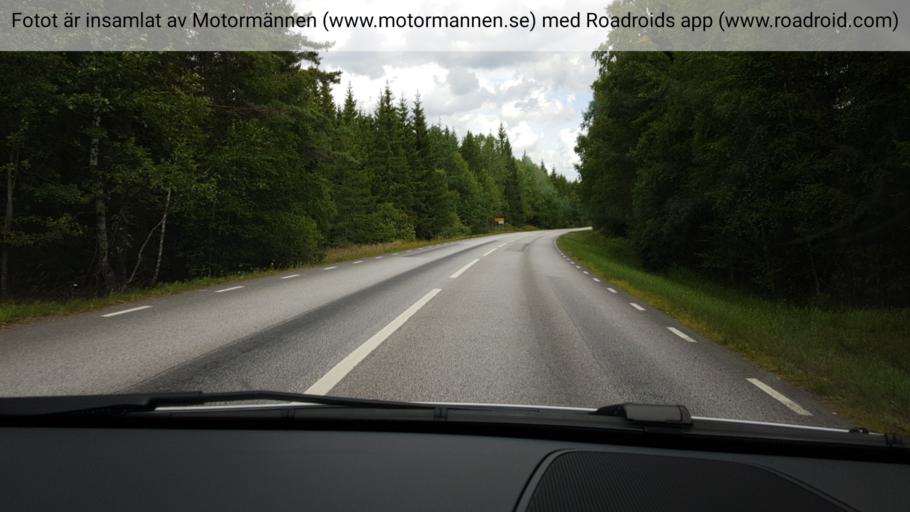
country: SE
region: Stockholm
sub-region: Sigtuna Kommun
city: Marsta
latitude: 59.7957
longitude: 18.0374
